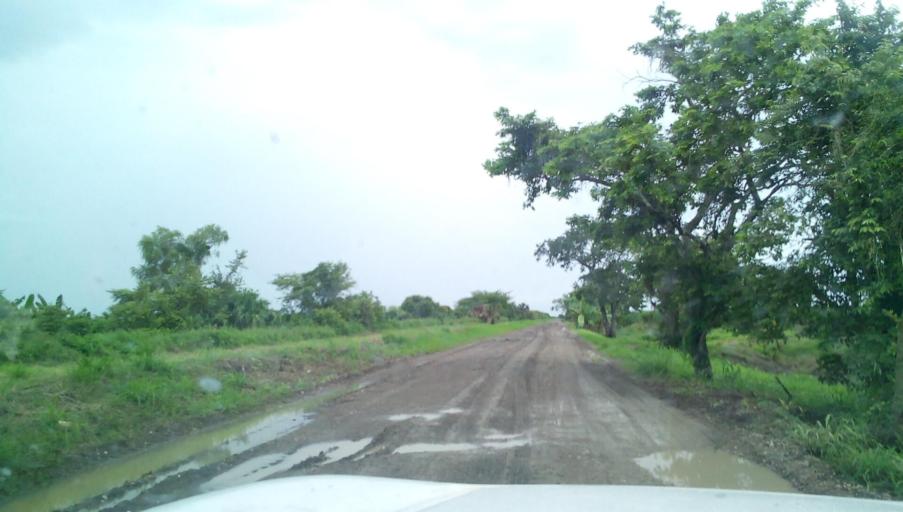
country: MX
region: Veracruz
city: Panuco
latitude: 21.8181
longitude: -98.1109
